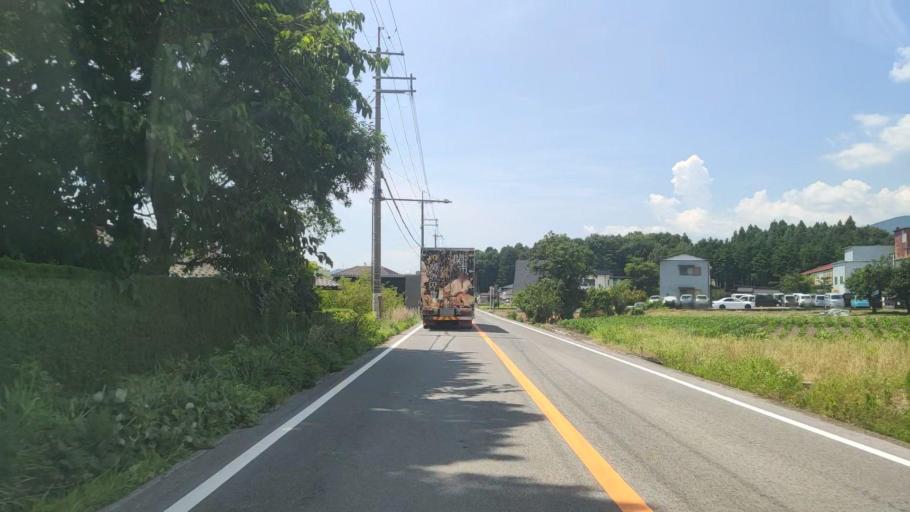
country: JP
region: Shiga Prefecture
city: Nagahama
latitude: 35.3779
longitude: 136.3791
